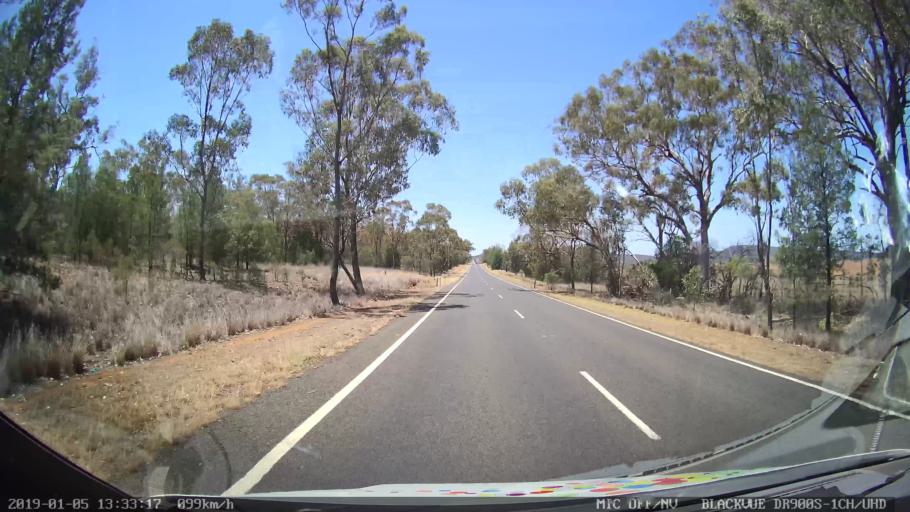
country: AU
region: New South Wales
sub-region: Gunnedah
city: Gunnedah
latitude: -31.0014
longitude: 150.1141
